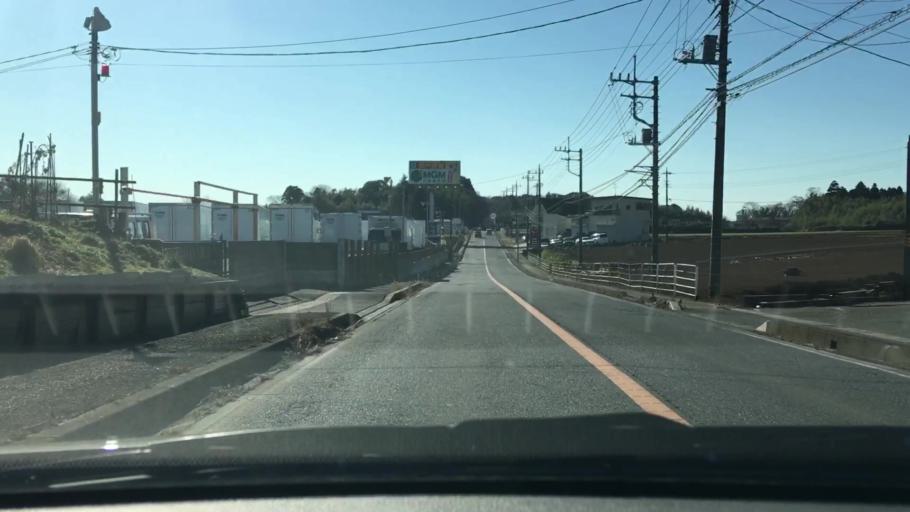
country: JP
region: Chiba
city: Shisui
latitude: 35.7031
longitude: 140.3130
